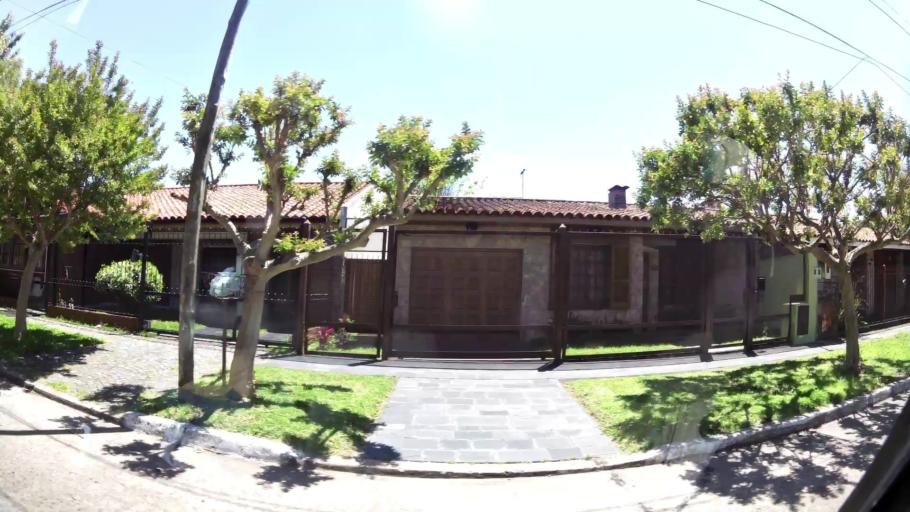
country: AR
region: Buenos Aires
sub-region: Partido de Quilmes
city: Quilmes
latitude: -34.7401
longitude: -58.2825
